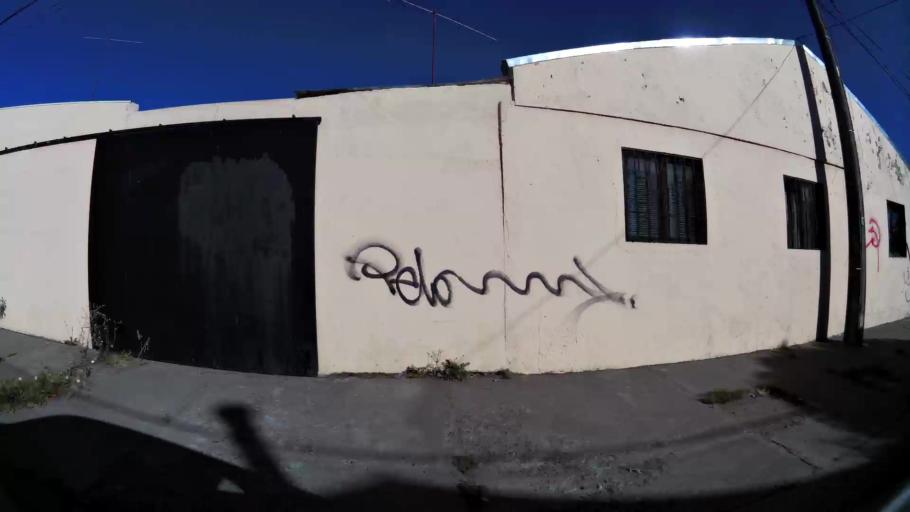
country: CL
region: O'Higgins
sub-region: Provincia de Cachapoal
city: Rancagua
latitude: -34.1787
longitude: -70.7238
